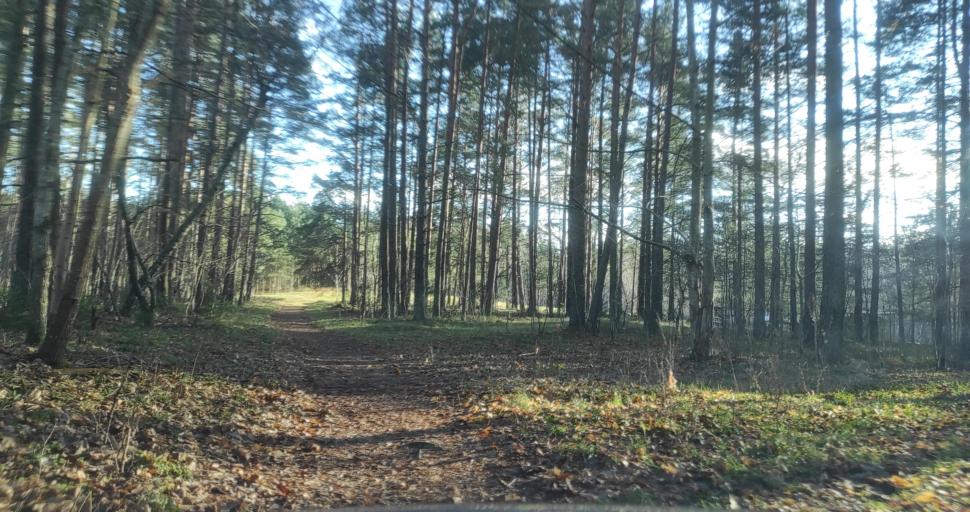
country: LV
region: Kuldigas Rajons
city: Kuldiga
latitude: 56.9610
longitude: 21.9306
